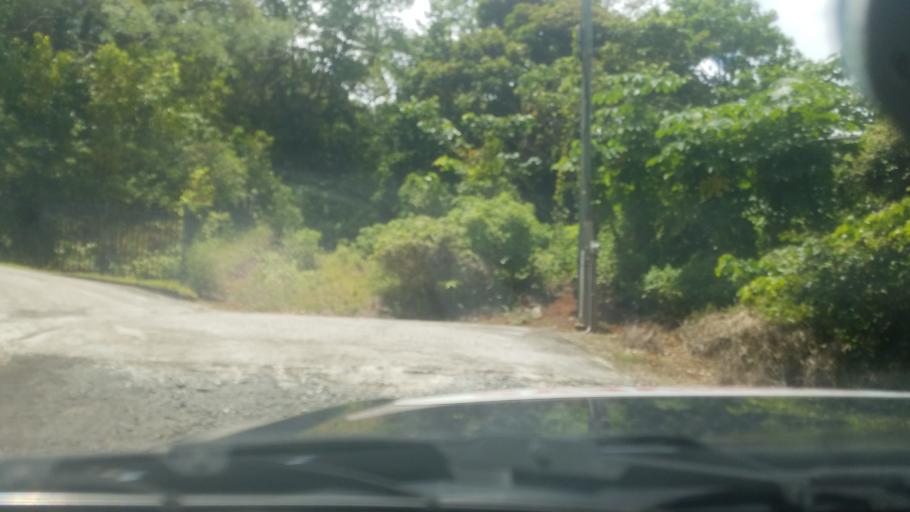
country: LC
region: Praslin
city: Praslin
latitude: 13.8730
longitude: -60.9162
